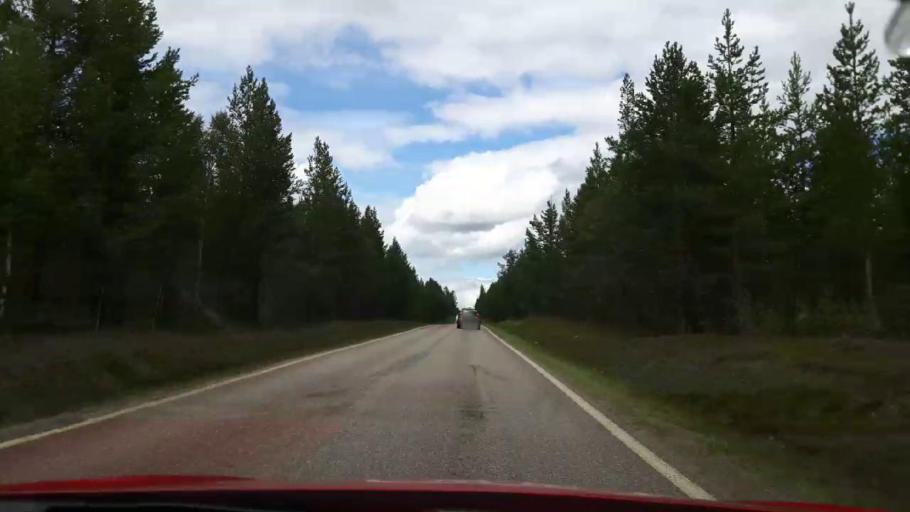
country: NO
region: Hedmark
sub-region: Trysil
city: Innbygda
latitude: 61.8399
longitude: 12.9562
